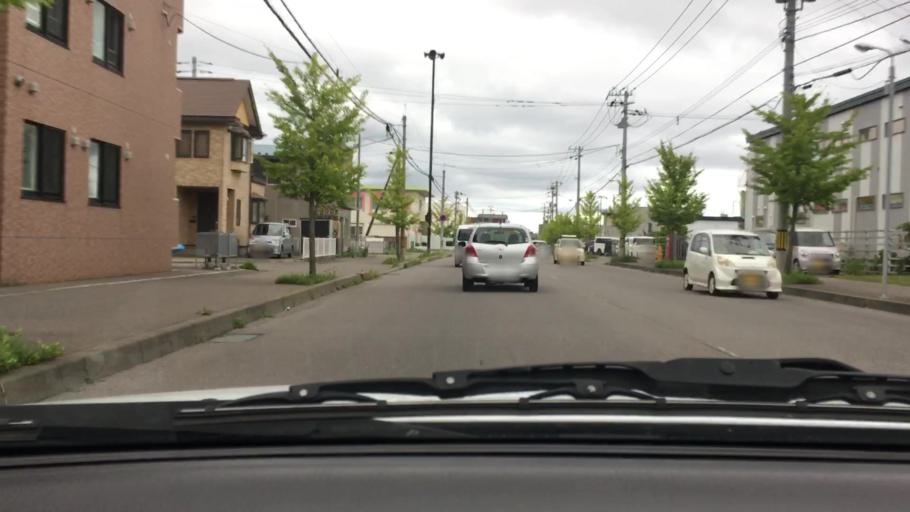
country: JP
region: Hokkaido
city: Hakodate
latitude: 41.7933
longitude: 140.7276
